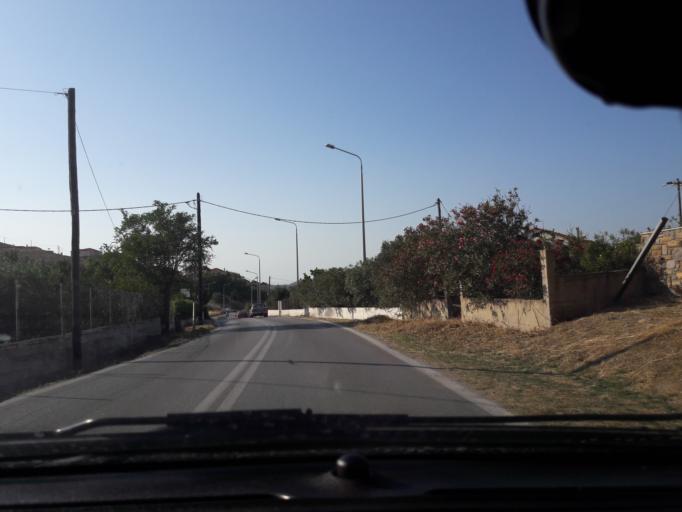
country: GR
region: North Aegean
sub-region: Nomos Lesvou
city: Myrina
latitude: 39.8653
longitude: 25.0739
